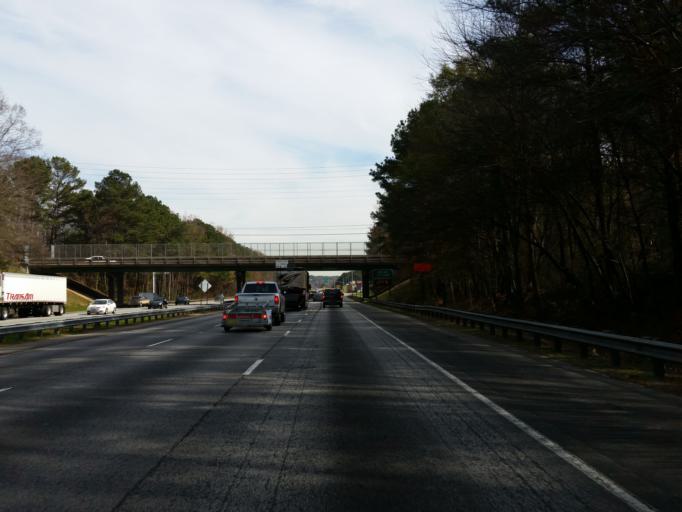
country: US
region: Georgia
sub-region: Douglas County
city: Lithia Springs
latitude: 33.7714
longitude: -84.6383
